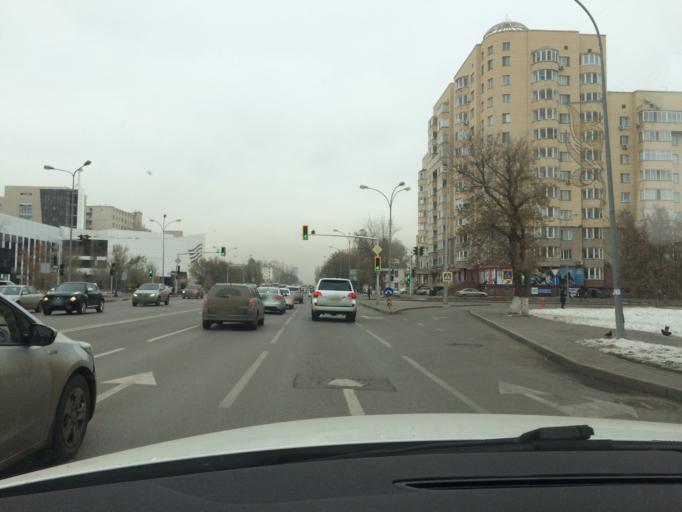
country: KZ
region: Astana Qalasy
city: Astana
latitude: 51.1722
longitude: 71.4122
